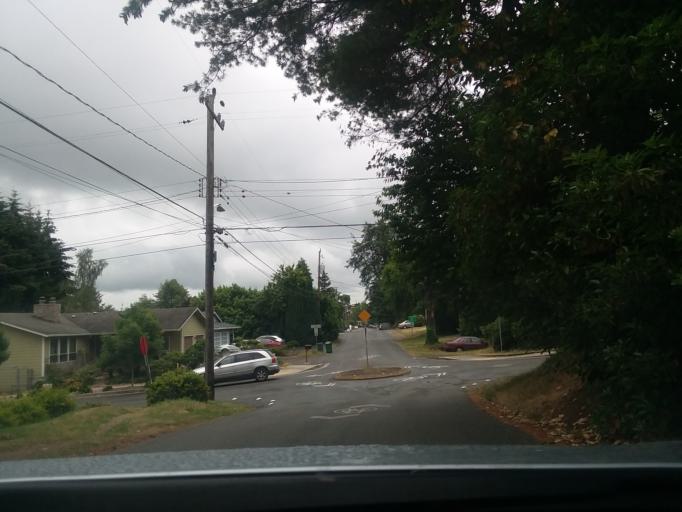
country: US
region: Washington
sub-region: King County
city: Lake Forest Park
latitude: 47.7232
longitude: -122.2991
